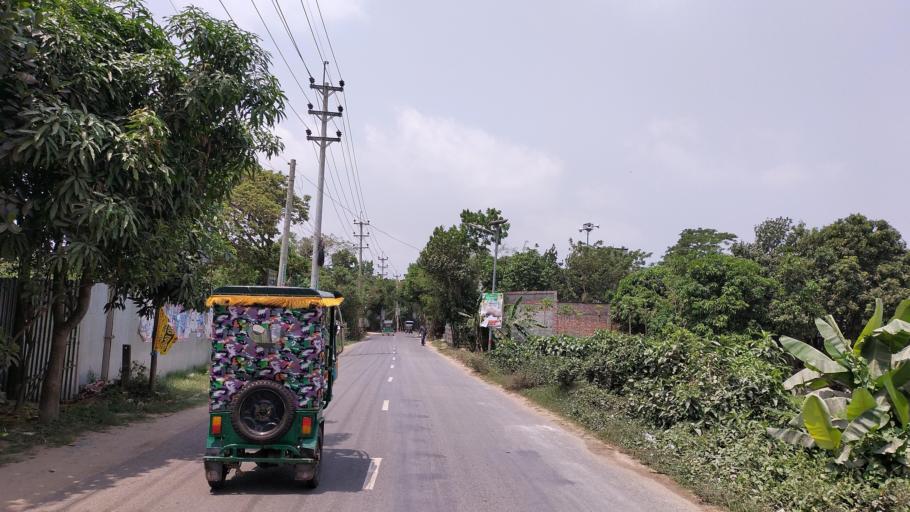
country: BD
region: Dhaka
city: Azimpur
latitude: 23.7288
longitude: 90.2920
